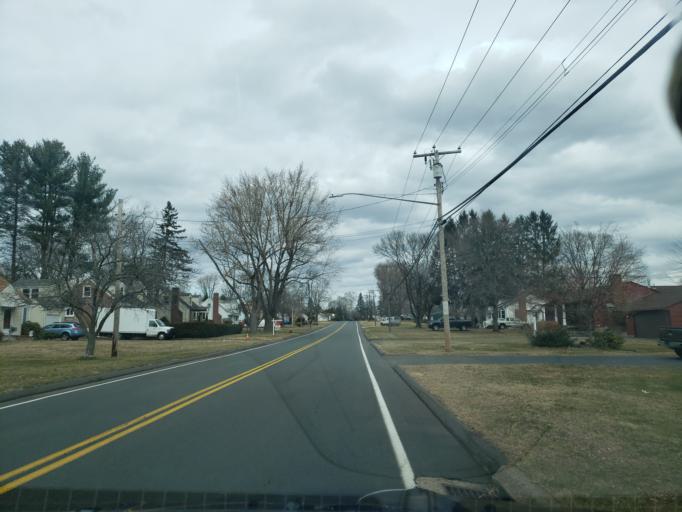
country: US
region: Connecticut
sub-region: Hartford County
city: Wethersfield
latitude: 41.6700
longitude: -72.6666
